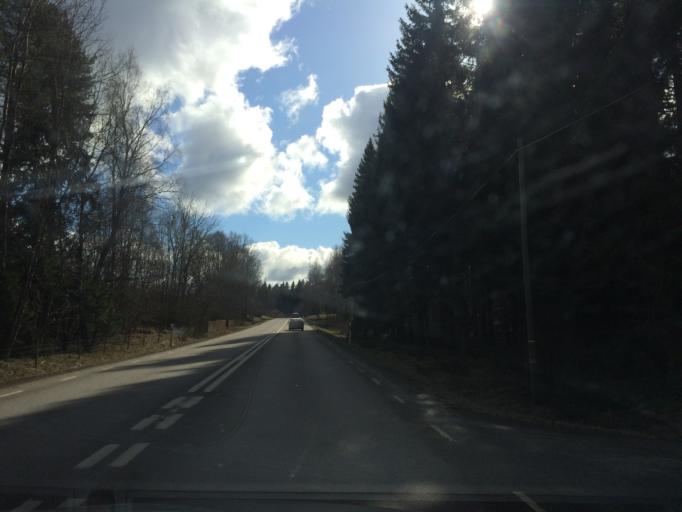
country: SE
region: Vaestra Goetaland
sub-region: Skara Kommun
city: Skara
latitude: 58.3222
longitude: 13.4342
